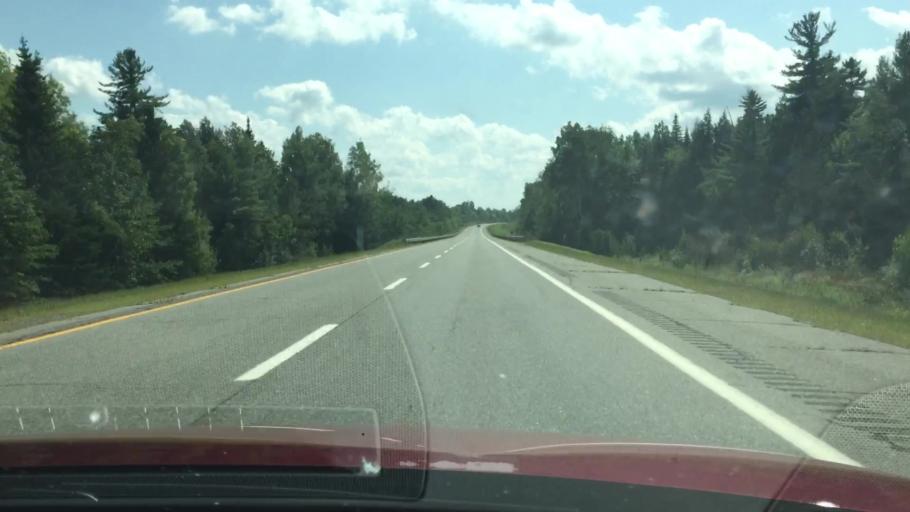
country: US
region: Maine
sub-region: Penobscot County
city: Lincoln
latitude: 45.4364
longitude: -68.5901
